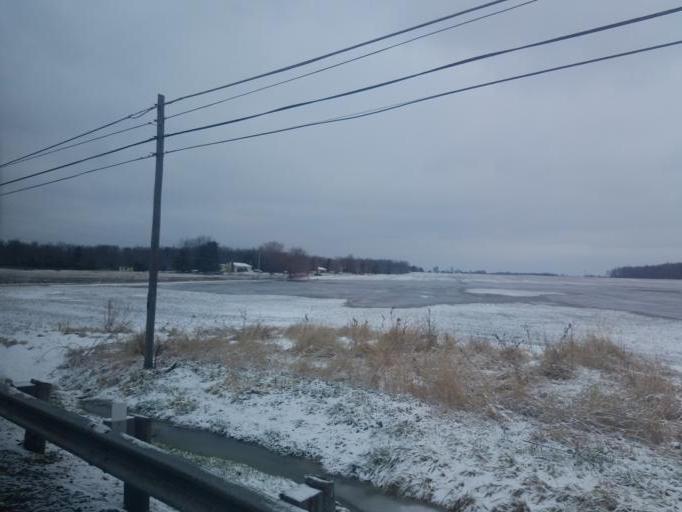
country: US
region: Ohio
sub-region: Licking County
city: Johnstown
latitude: 40.1807
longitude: -82.7418
